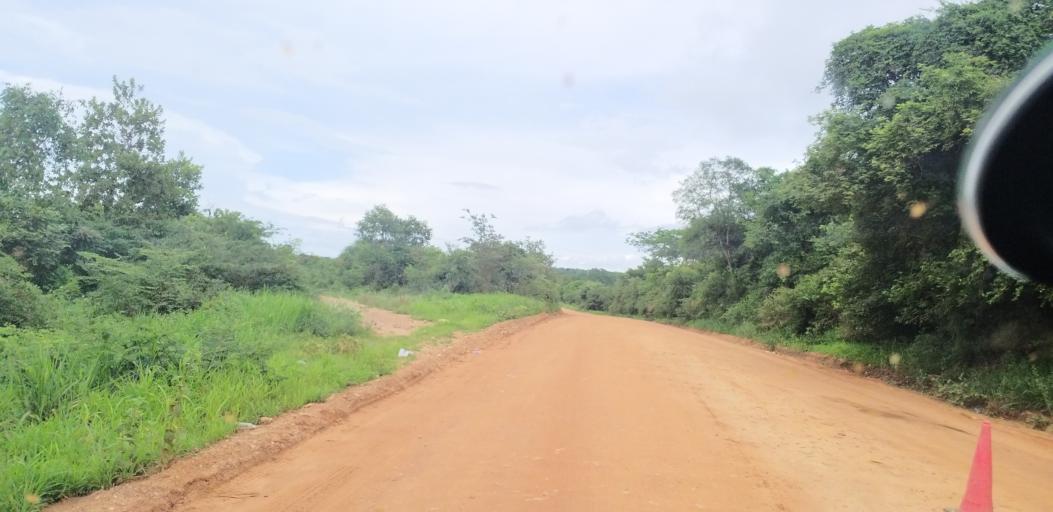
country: ZM
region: Lusaka
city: Lusaka
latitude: -15.1921
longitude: 28.4447
